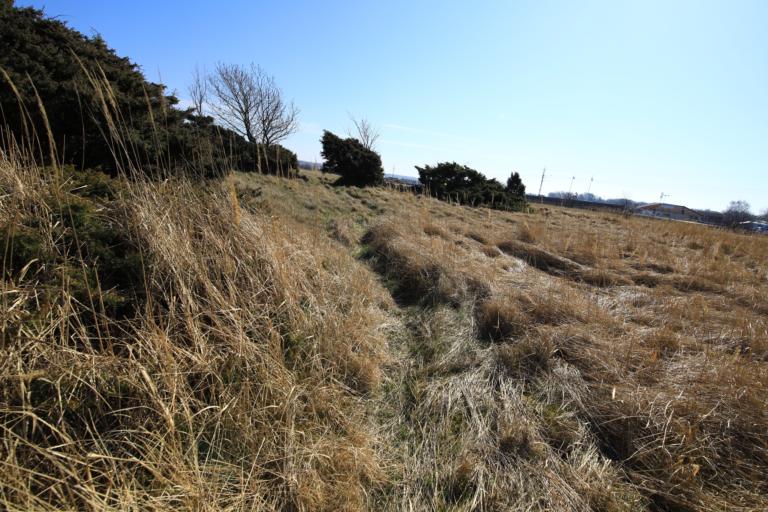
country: SE
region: Halland
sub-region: Varbergs Kommun
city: Varberg
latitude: 57.0890
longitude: 12.2483
